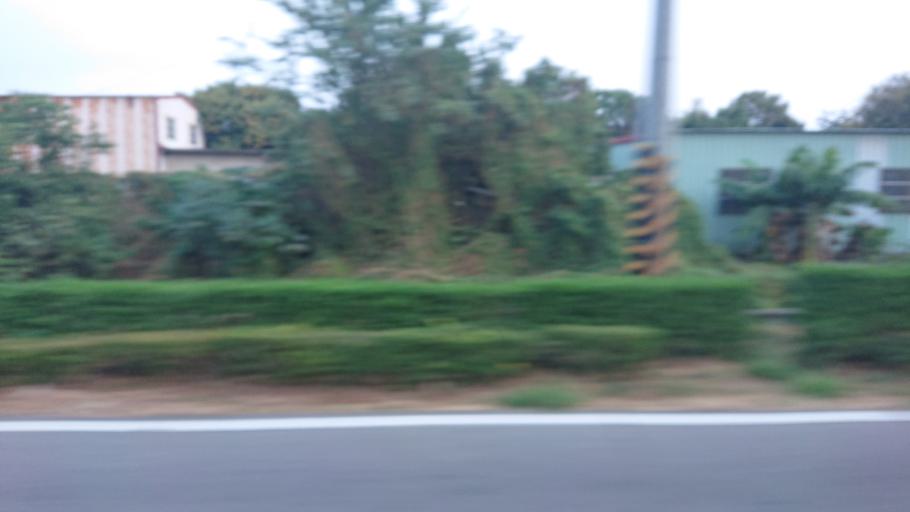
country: TW
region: Fukien
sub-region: Kinmen
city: Jincheng
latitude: 24.4578
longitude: 118.3215
